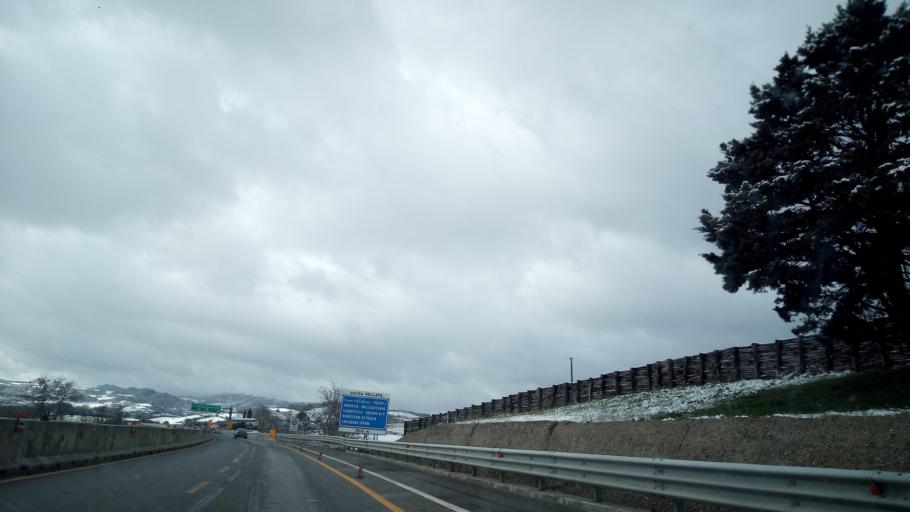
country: IT
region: Campania
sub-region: Provincia di Avellino
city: Scampitella
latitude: 41.0619
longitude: 15.2990
